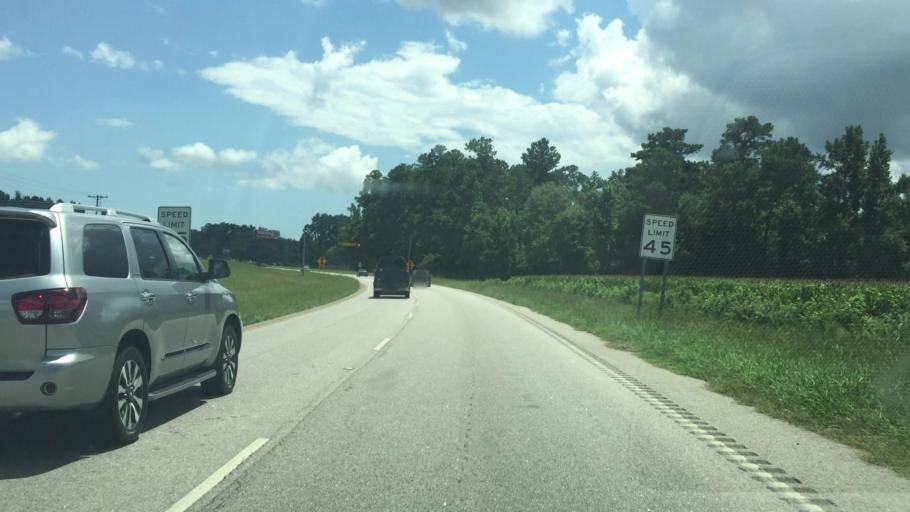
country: US
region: South Carolina
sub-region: Horry County
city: North Myrtle Beach
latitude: 33.9427
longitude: -78.7355
